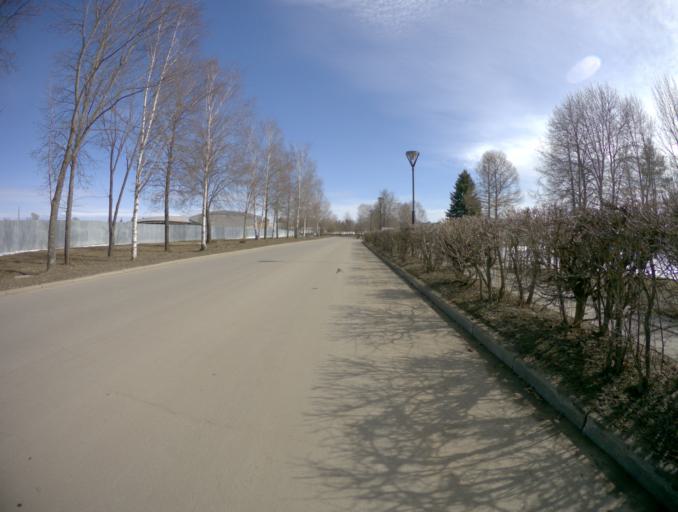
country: RU
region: Vladimir
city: Suzdal'
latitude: 56.4317
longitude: 40.4224
